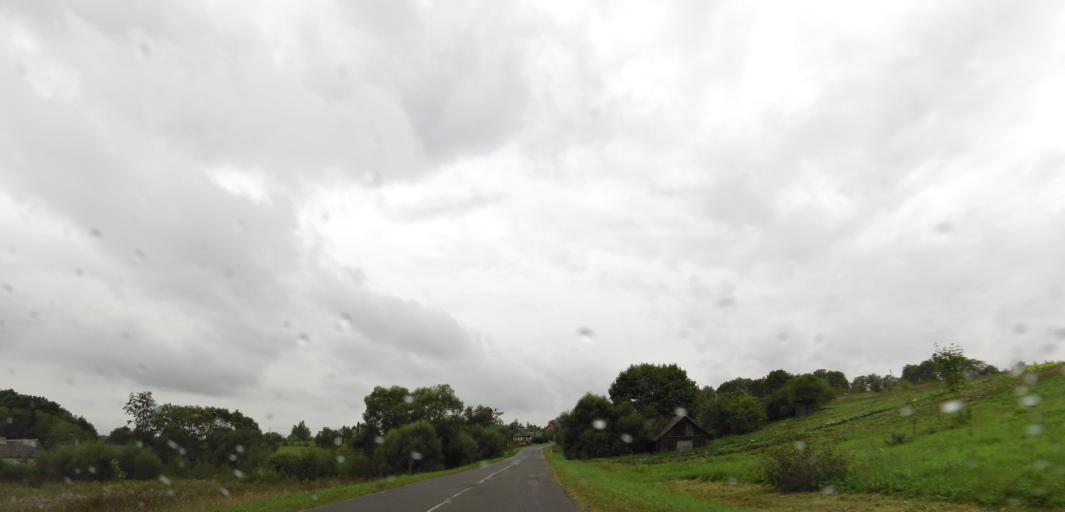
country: LT
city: Sirvintos
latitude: 55.0749
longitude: 25.0655
